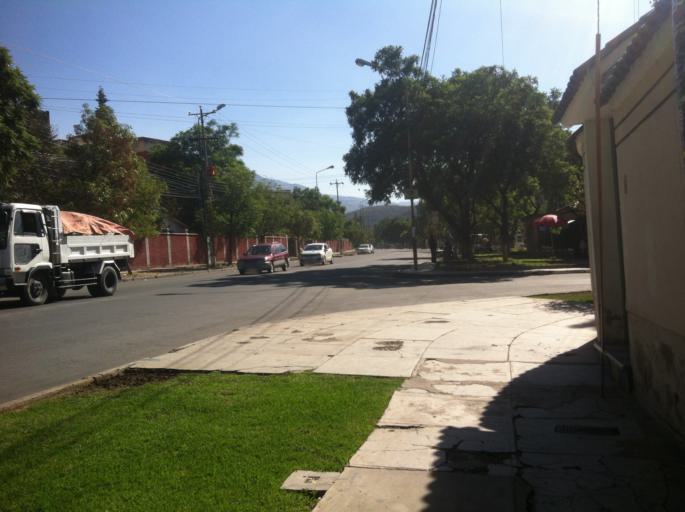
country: BO
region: Cochabamba
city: Cochabamba
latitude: -17.3808
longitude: -66.1487
